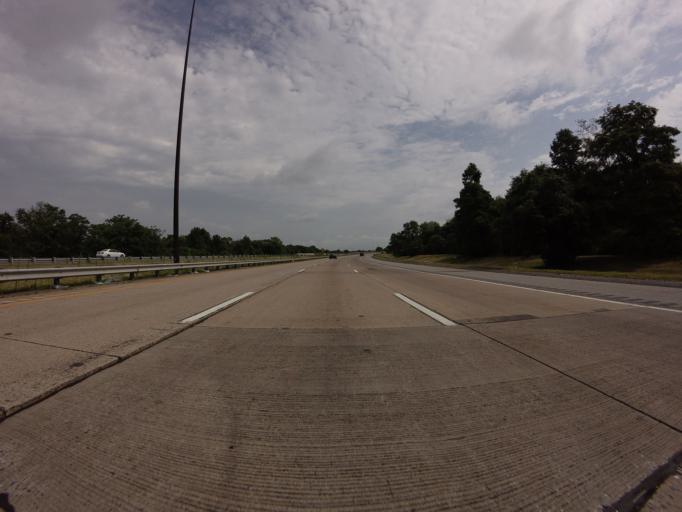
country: US
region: Delaware
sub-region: New Castle County
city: Newport
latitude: 39.7095
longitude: -75.5871
